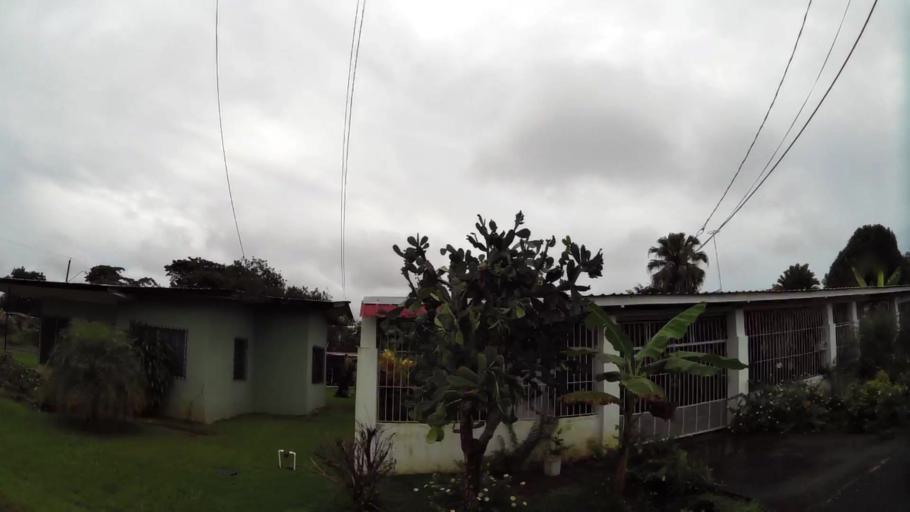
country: PA
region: Chiriqui
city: David
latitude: 8.4251
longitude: -82.4504
